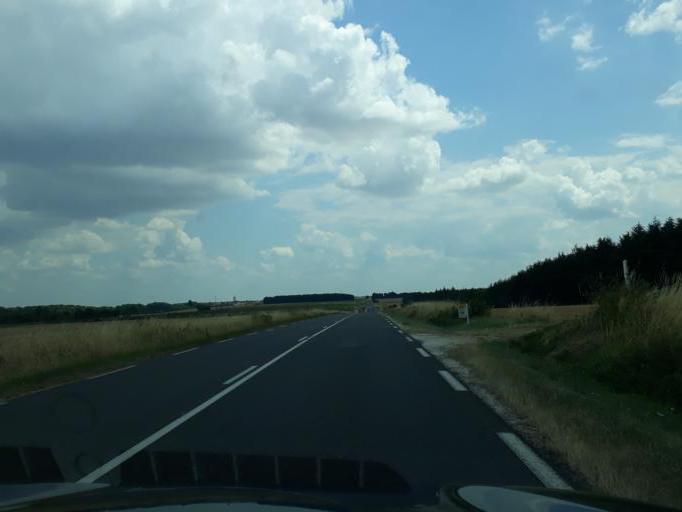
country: FR
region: Centre
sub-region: Departement du Cher
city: Avord
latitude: 47.0371
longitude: 2.6043
